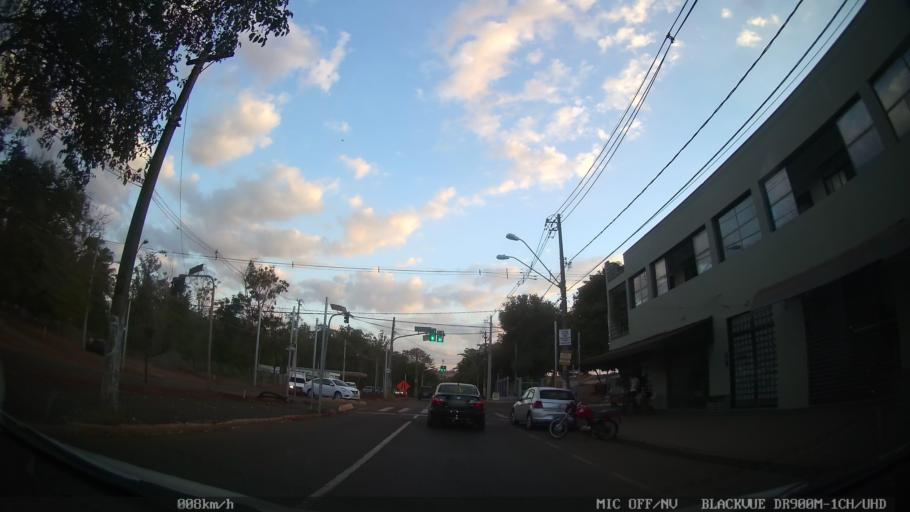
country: BR
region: Sao Paulo
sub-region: Ribeirao Preto
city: Ribeirao Preto
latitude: -21.1608
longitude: -47.7877
